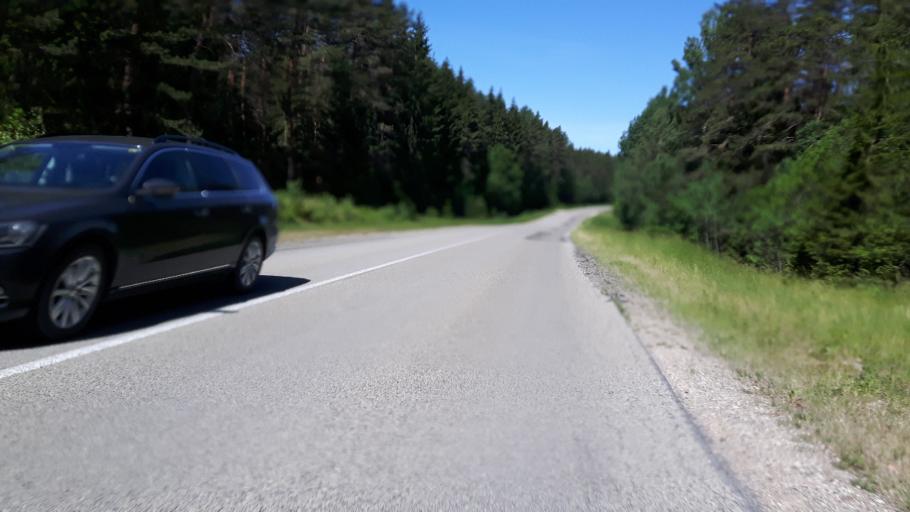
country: LV
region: Tukuma Rajons
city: Tukums
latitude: 57.0062
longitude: 23.0642
